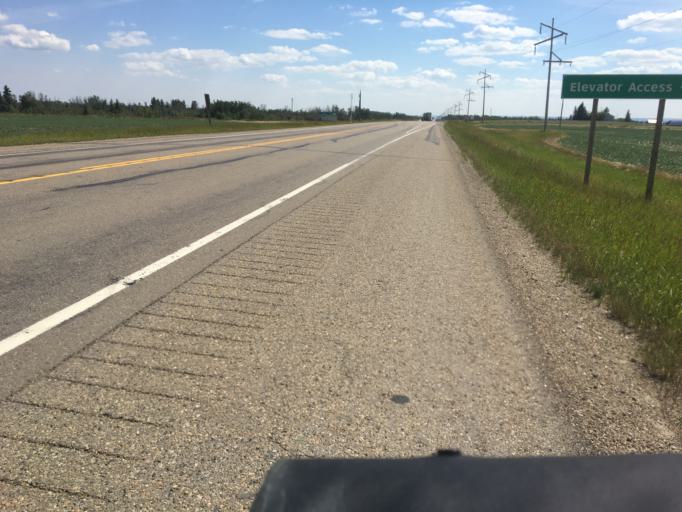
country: CA
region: Alberta
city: Spirit River
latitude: 55.7248
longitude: -118.6987
